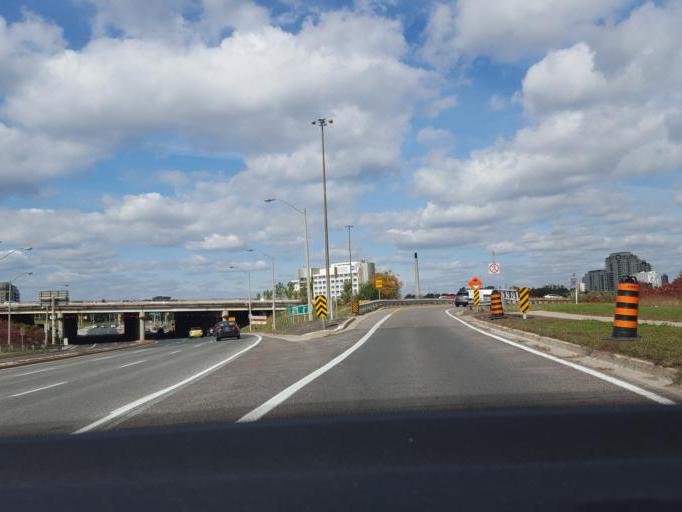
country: CA
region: Ontario
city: Willowdale
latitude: 43.7647
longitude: -79.3618
